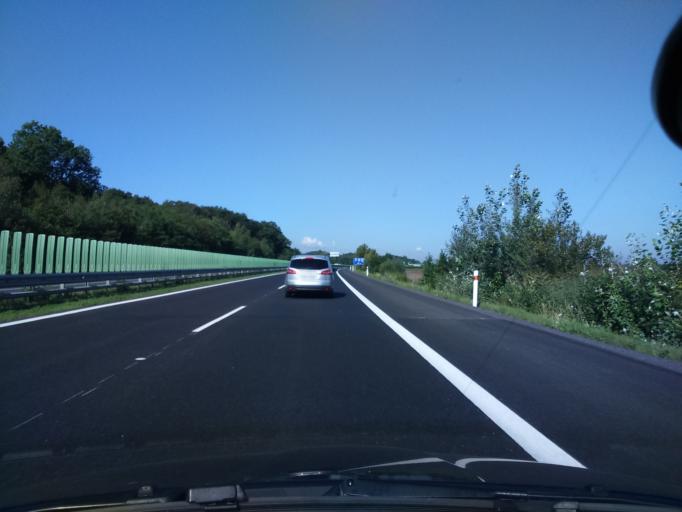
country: CZ
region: Central Bohemia
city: Poricany
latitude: 50.1292
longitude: 14.8777
